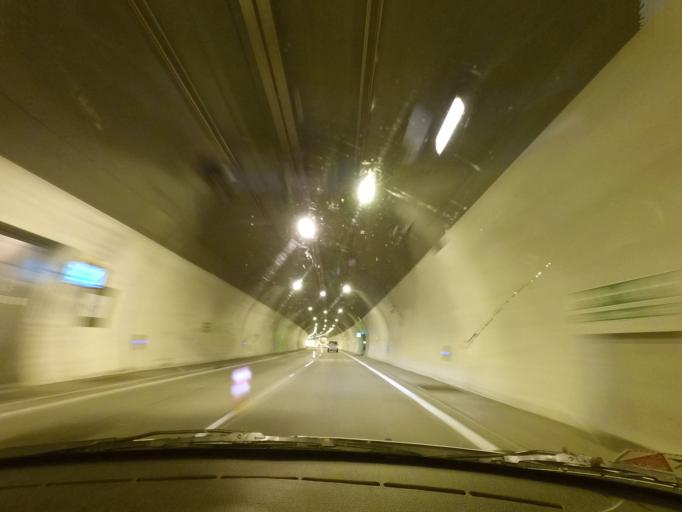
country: CZ
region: Ustecky
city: Libouchec
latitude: 50.7449
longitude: 14.0066
